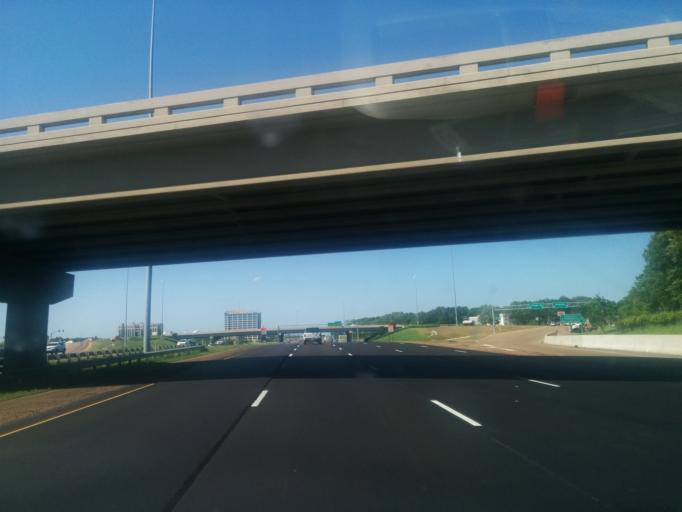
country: US
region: Mississippi
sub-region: Madison County
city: Ridgeland
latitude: 32.4279
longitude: -90.1437
